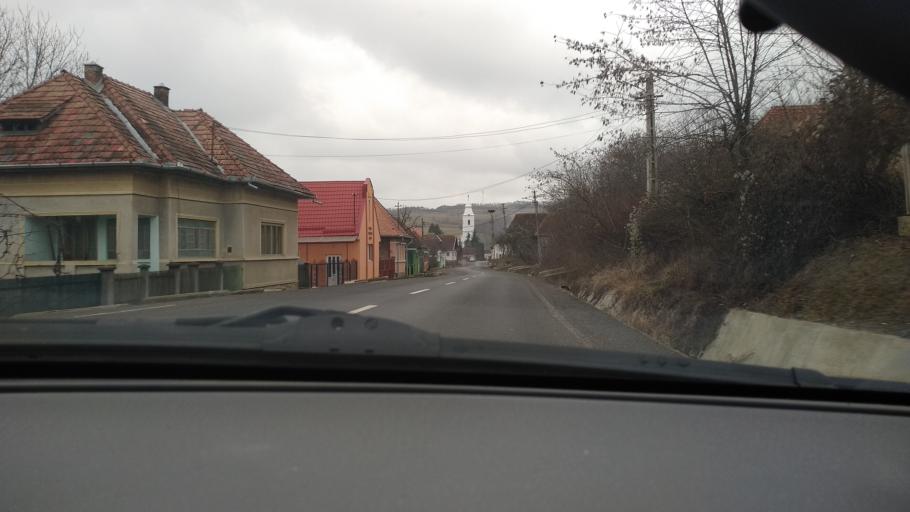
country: RO
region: Mures
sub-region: Comuna Magherani
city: Magherani
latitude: 46.5640
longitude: 24.9088
